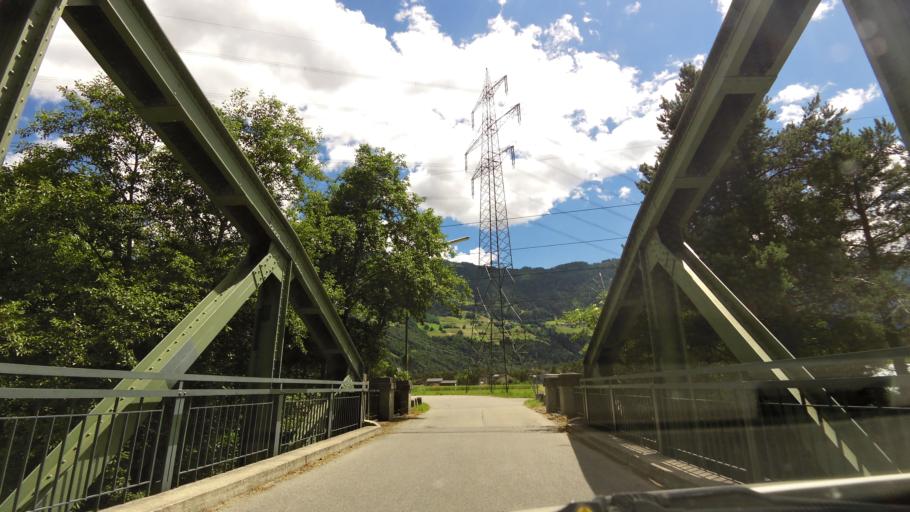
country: AT
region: Tyrol
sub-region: Politischer Bezirk Imst
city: Haiming
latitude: 47.2586
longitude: 10.8750
